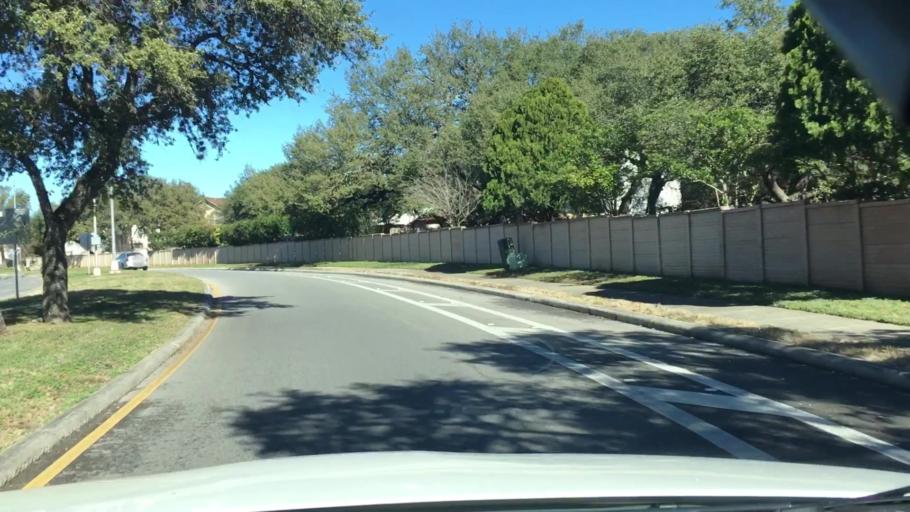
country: US
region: Texas
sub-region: Bexar County
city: Hollywood Park
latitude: 29.6004
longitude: -98.4569
